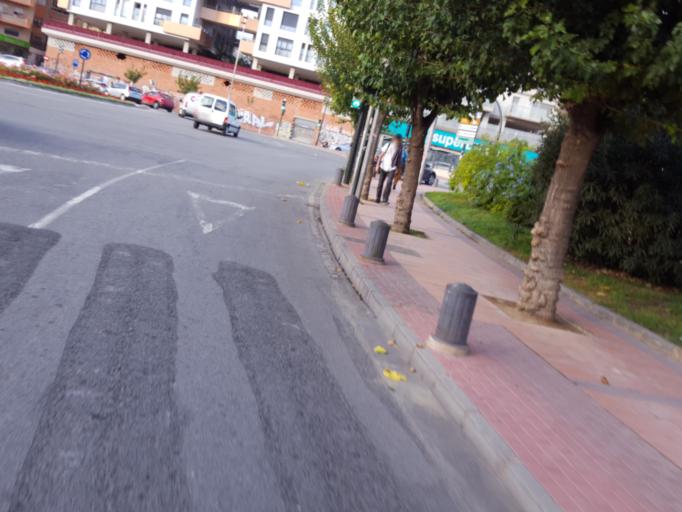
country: ES
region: Murcia
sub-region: Murcia
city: Murcia
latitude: 37.9926
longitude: -1.1413
